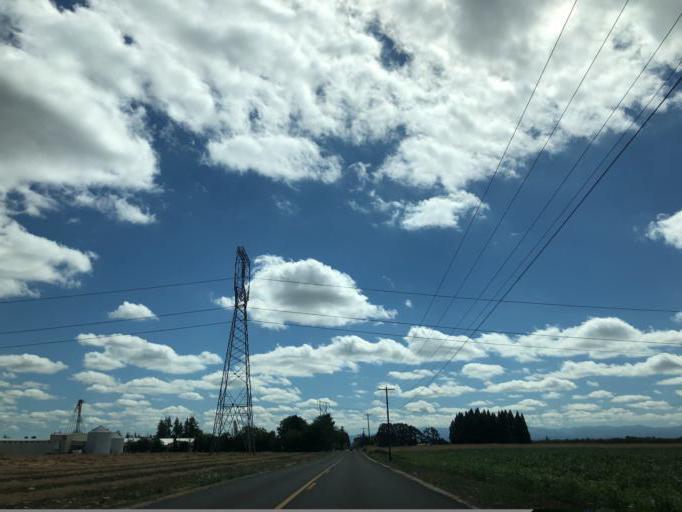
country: US
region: Oregon
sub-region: Marion County
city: Hubbard
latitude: 45.1727
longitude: -122.7295
